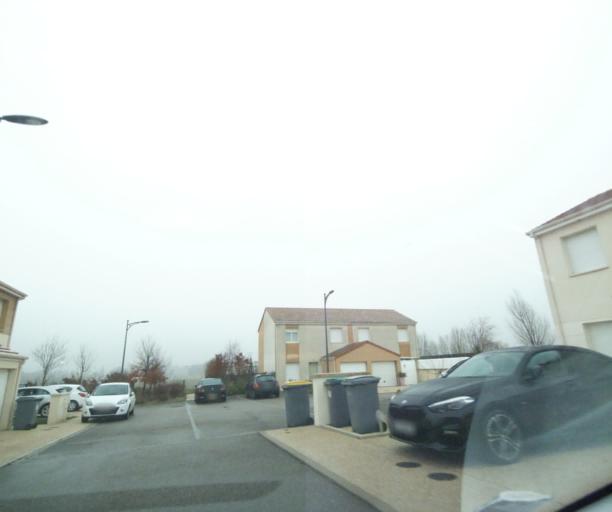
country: FR
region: Ile-de-France
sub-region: Departement de Seine-et-Marne
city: Othis
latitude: 49.0656
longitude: 2.6783
